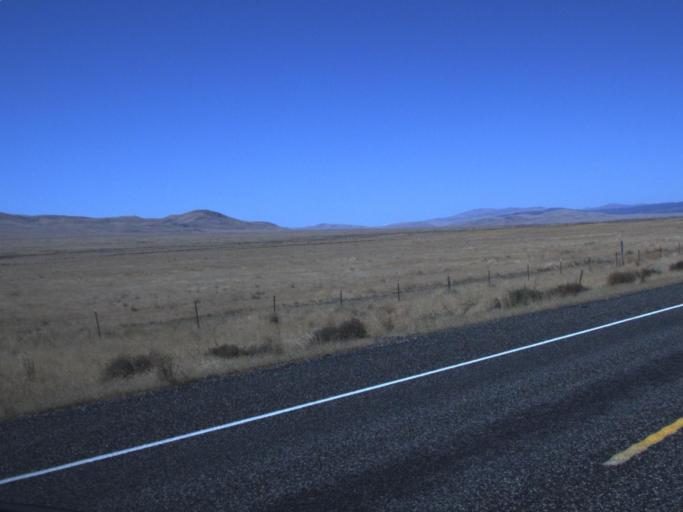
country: US
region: Washington
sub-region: Benton County
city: Benton City
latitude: 46.4435
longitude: -119.4933
